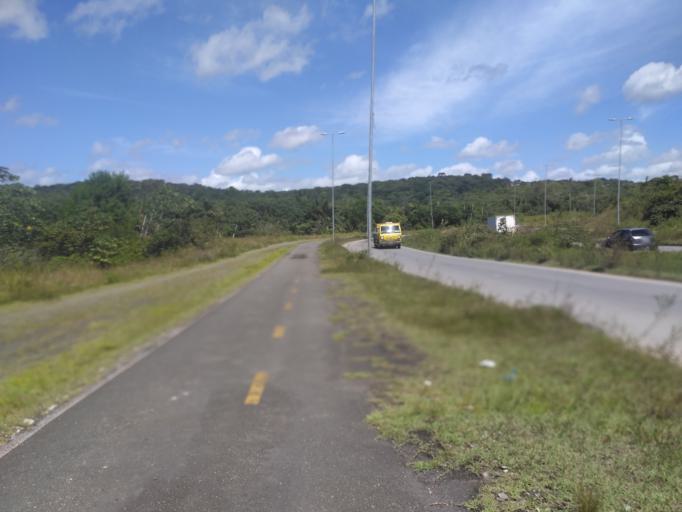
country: BR
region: Pernambuco
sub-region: Sao Lourenco Da Mata
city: Sao Lourenco da Mata
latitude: -8.0432
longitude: -34.9978
